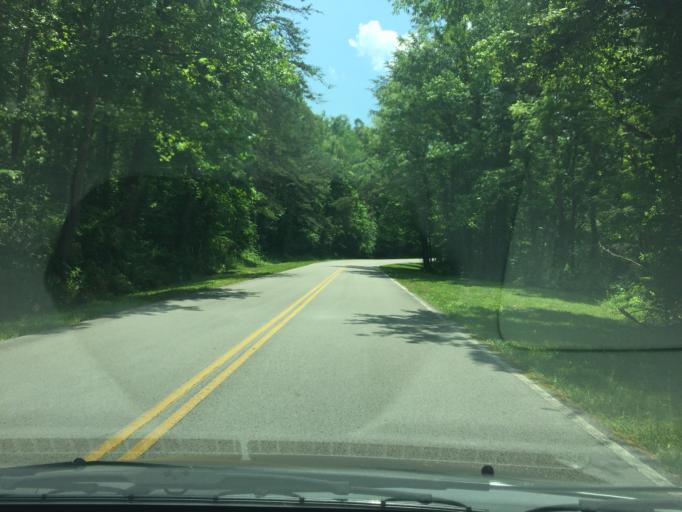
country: US
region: Tennessee
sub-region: Hamilton County
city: Lookout Mountain
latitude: 35.0431
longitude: -85.4238
